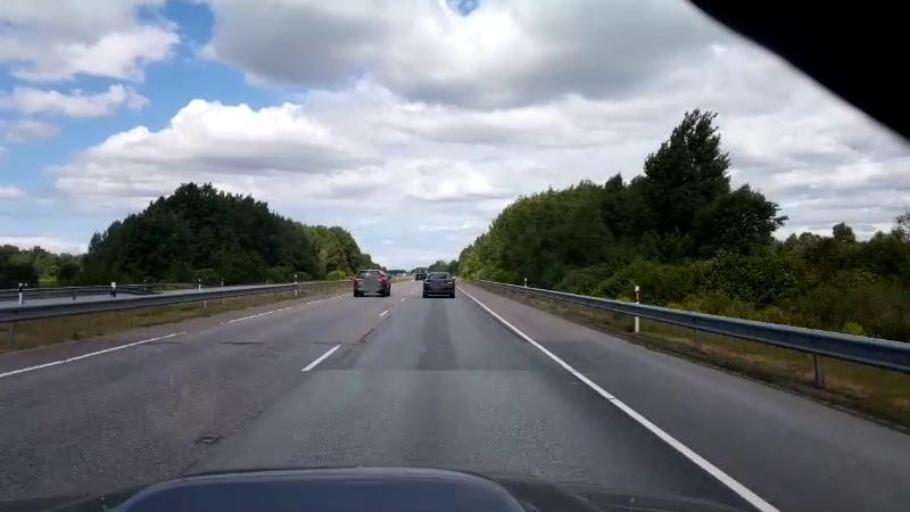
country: EE
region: Harju
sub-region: Saue linn
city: Saue
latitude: 59.2612
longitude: 24.5105
